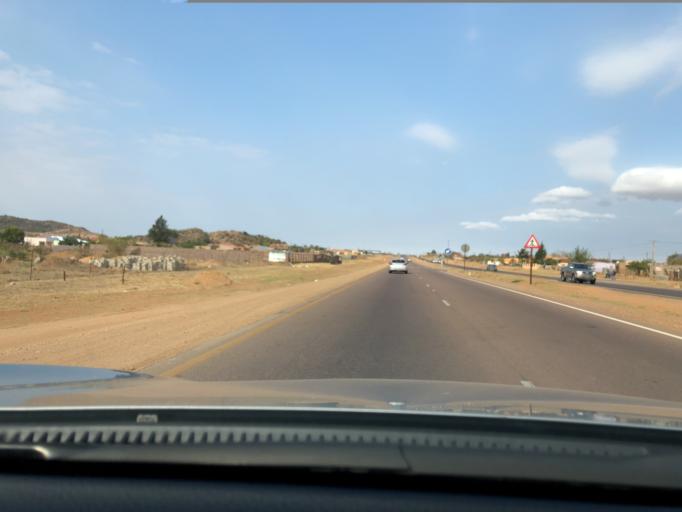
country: ZA
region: Limpopo
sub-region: Capricorn District Municipality
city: Mankoeng
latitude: -23.8917
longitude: 29.6542
